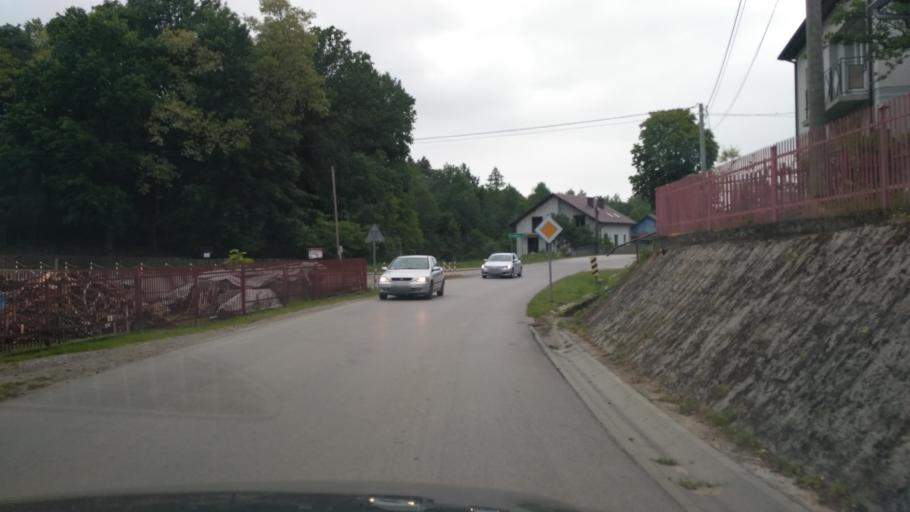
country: PL
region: Subcarpathian Voivodeship
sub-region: Powiat kolbuszowski
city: Niwiska
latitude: 50.2179
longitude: 21.6324
